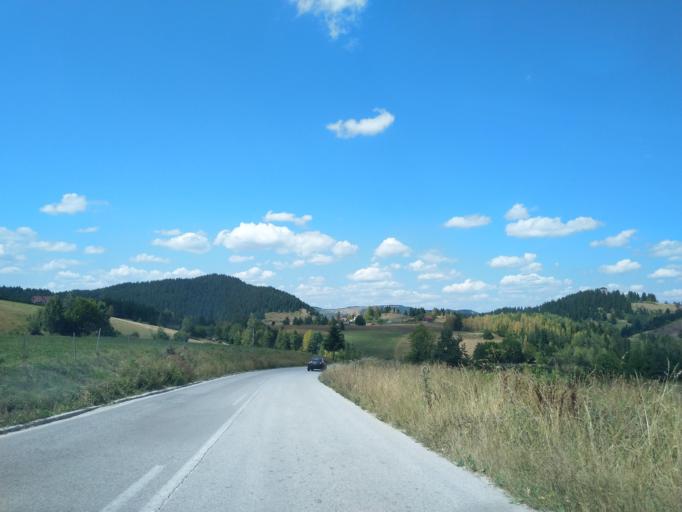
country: RS
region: Central Serbia
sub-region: Zlatiborski Okrug
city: Nova Varos
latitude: 43.4230
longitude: 19.8276
